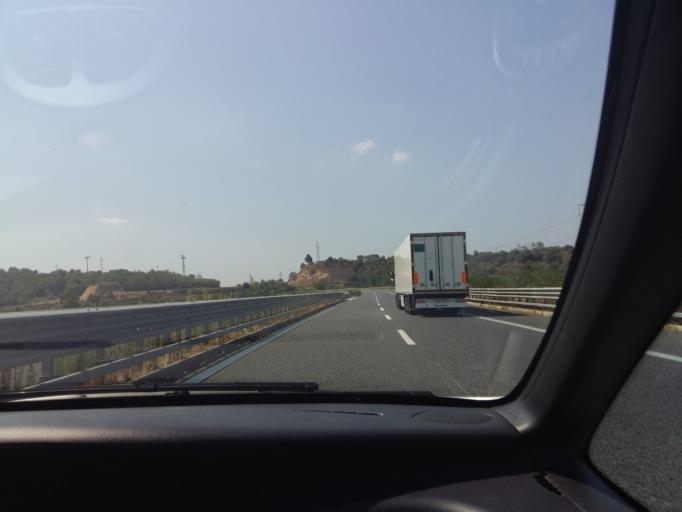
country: IT
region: Calabria
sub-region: Provincia di Reggio Calabria
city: Rosarno
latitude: 38.4880
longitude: 16.0068
